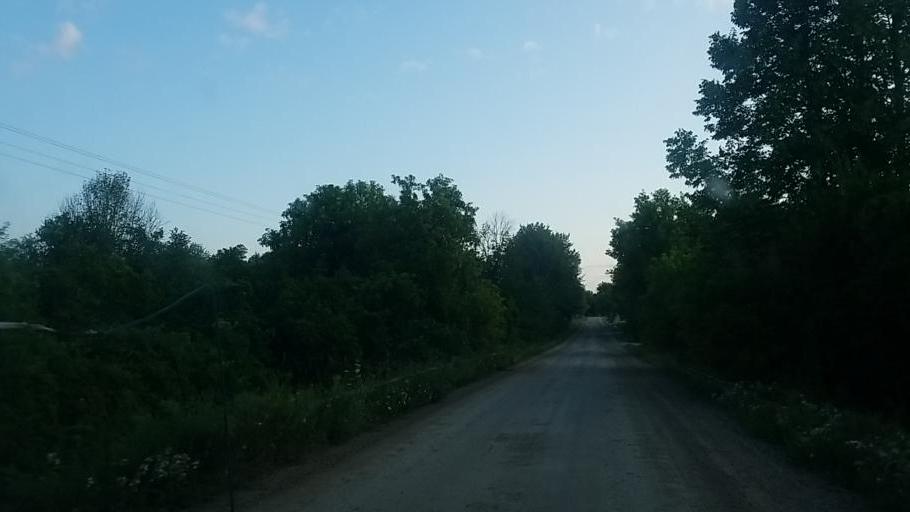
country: US
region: Michigan
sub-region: Osceola County
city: Evart
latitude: 43.9101
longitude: -85.2066
